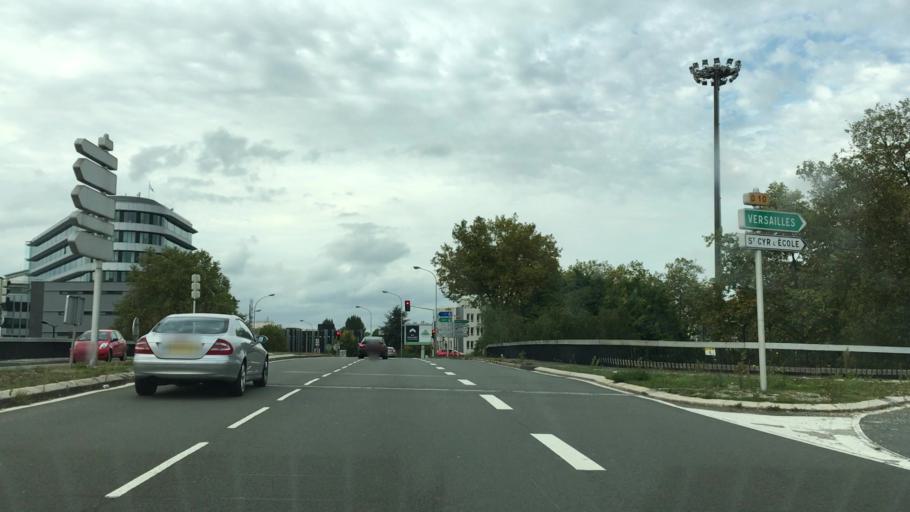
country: FR
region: Ile-de-France
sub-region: Departement des Yvelines
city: Saint-Cyr-l'Ecole
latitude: 48.7894
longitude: 2.0482
